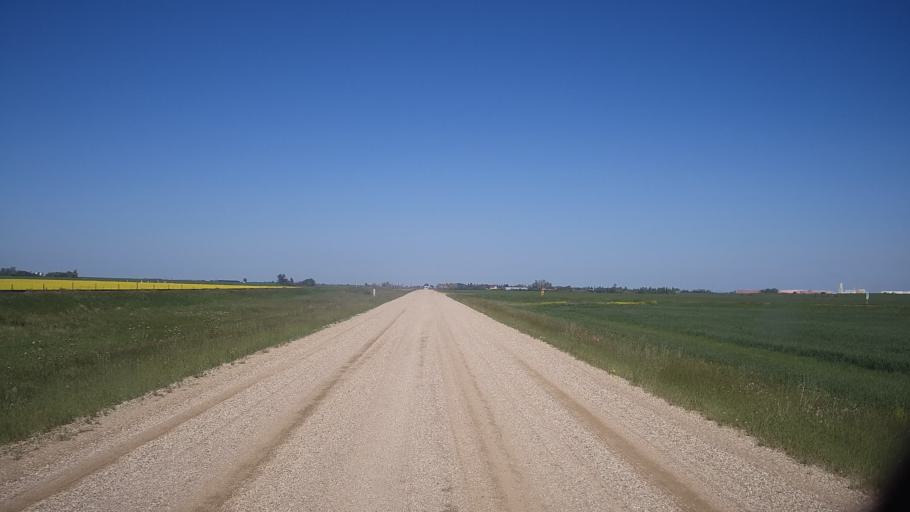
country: CA
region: Saskatchewan
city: Watrous
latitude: 51.8808
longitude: -106.0218
